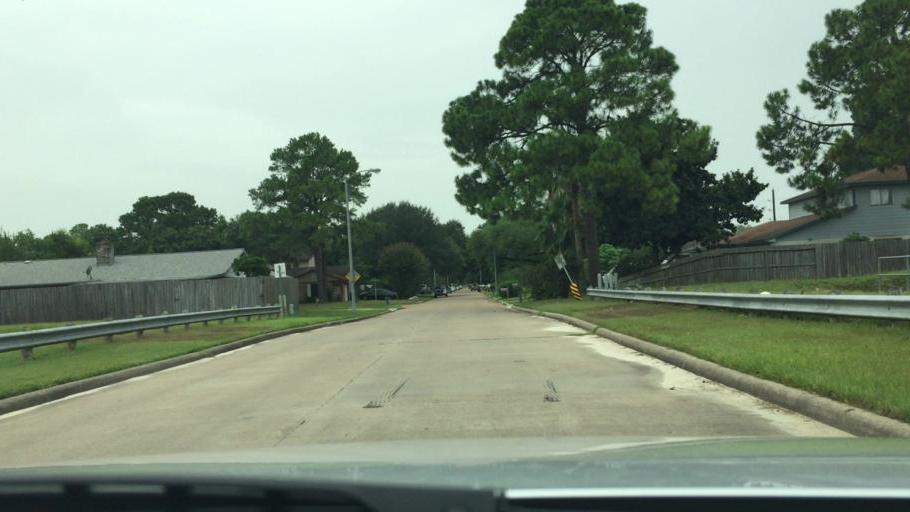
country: US
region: Texas
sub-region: Harris County
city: Hudson
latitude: 29.9071
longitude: -95.5162
